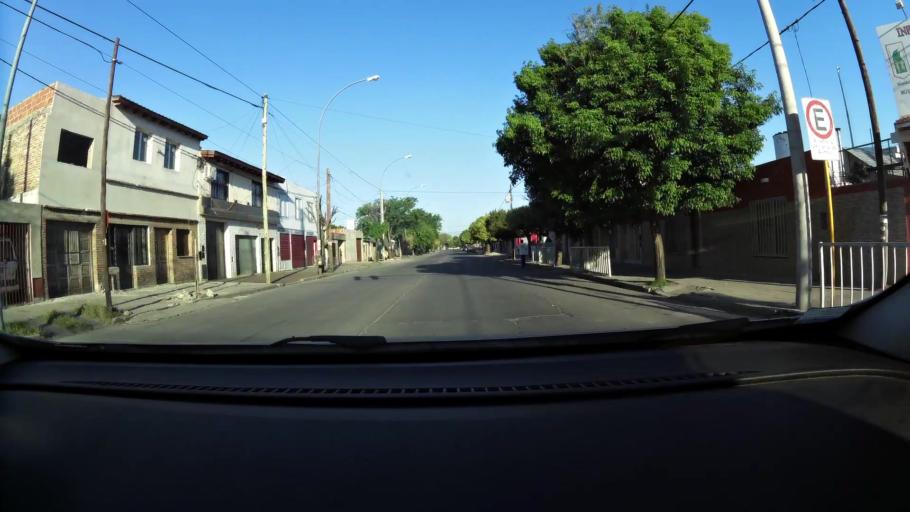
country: AR
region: Cordoba
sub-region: Departamento de Capital
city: Cordoba
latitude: -31.3759
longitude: -64.2016
